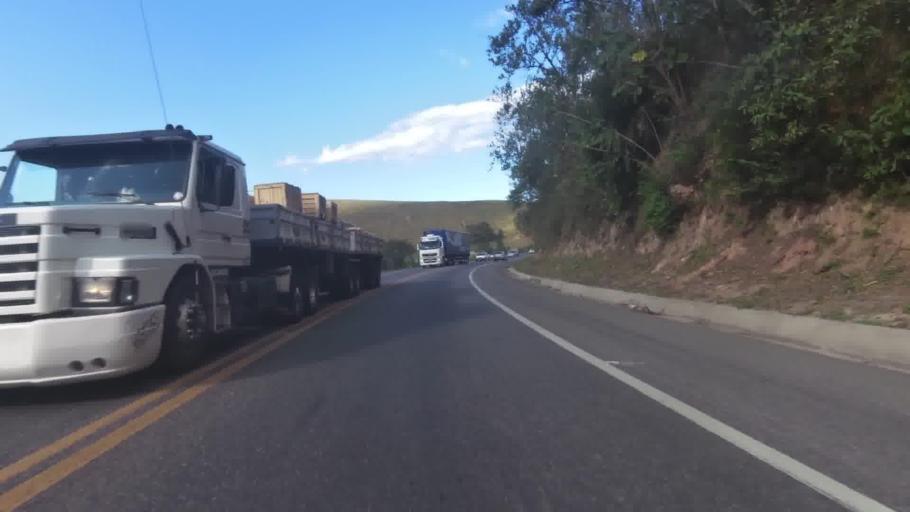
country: BR
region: Espirito Santo
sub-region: Rio Novo Do Sul
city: Rio Novo do Sul
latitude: -20.8645
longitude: -40.8861
